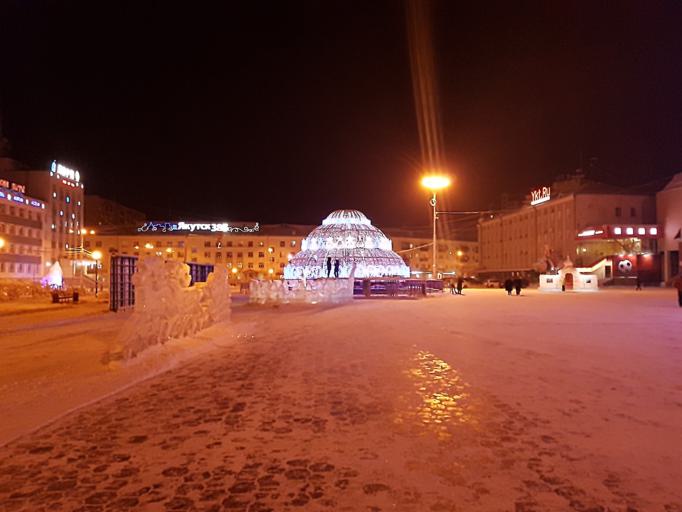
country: RU
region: Sakha
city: Yakutsk
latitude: 62.0340
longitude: 129.7435
